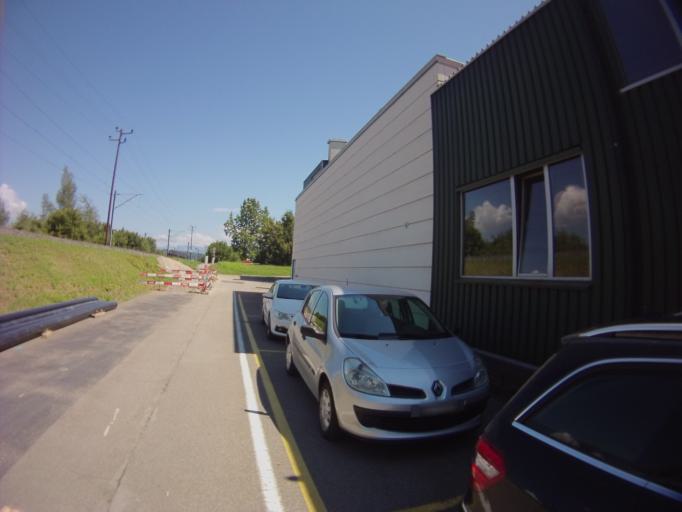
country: CH
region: Saint Gallen
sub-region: Wahlkreis See-Gaster
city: Jona
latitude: 47.2233
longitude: 8.8462
